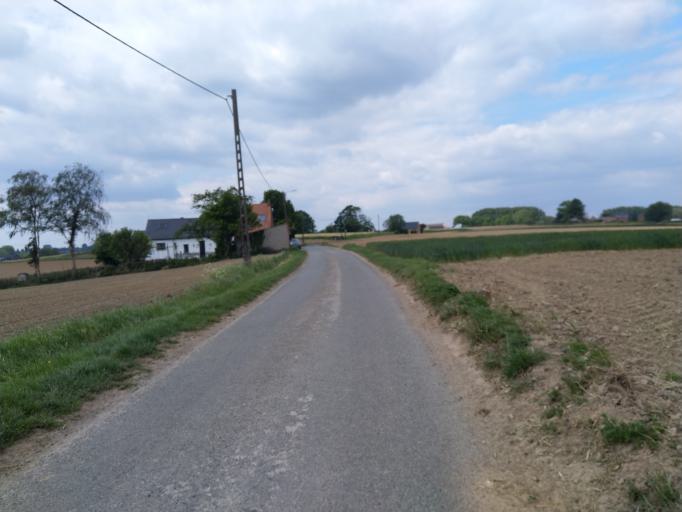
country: BE
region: Wallonia
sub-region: Province du Hainaut
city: Enghien
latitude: 50.6491
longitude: 4.0271
